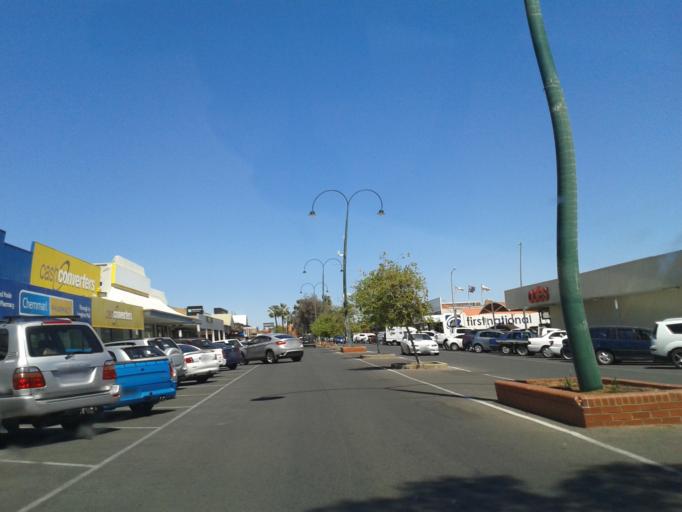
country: AU
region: Victoria
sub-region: Mildura Shire
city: Mildura
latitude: -34.1835
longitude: 142.1603
